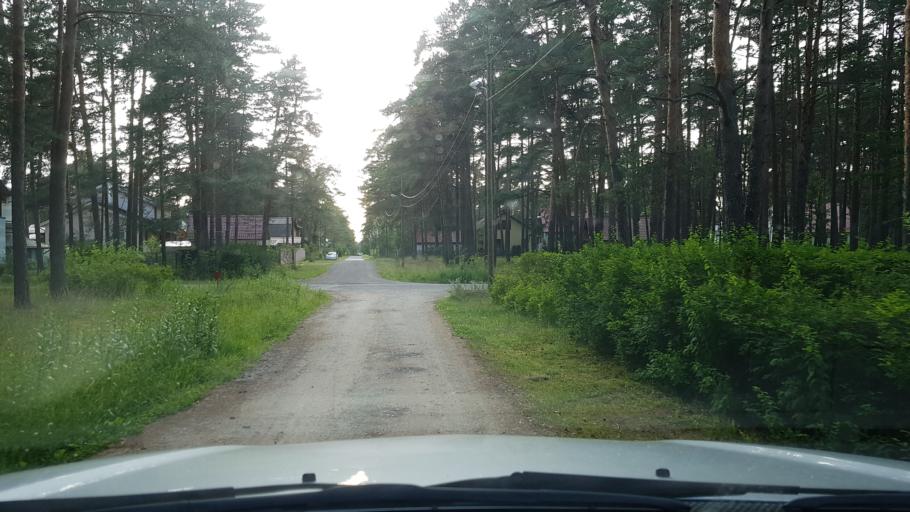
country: EE
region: Ida-Virumaa
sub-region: Narva-Joesuu linn
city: Narva-Joesuu
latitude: 59.4535
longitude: 28.0604
